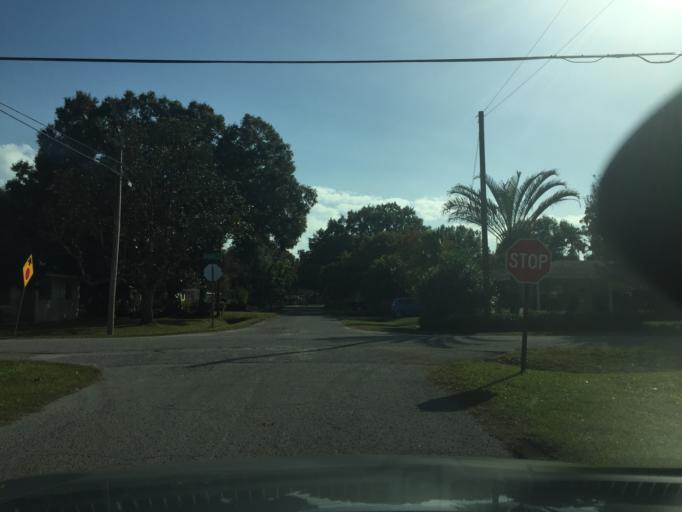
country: US
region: Florida
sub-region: Hillsborough County
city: Tampa
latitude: 27.9499
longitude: -82.4944
